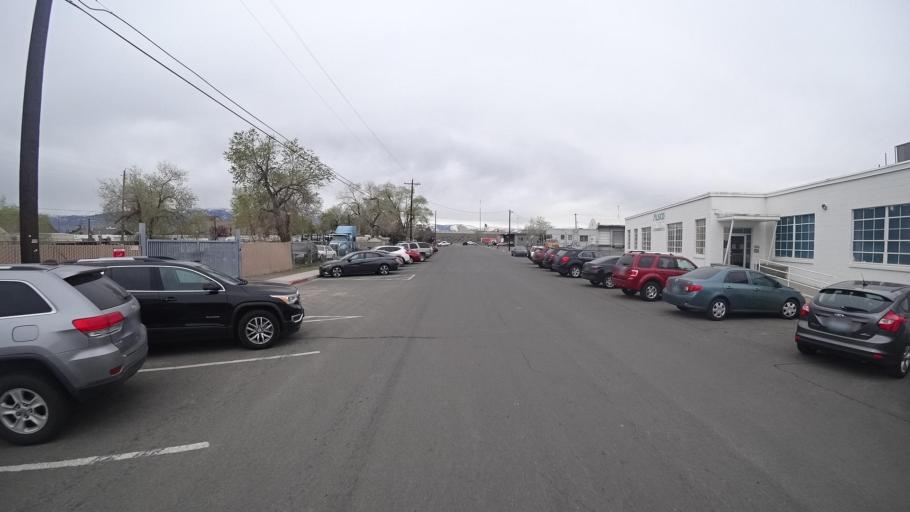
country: US
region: Nevada
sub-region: Washoe County
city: Reno
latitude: 39.5356
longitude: -119.7839
